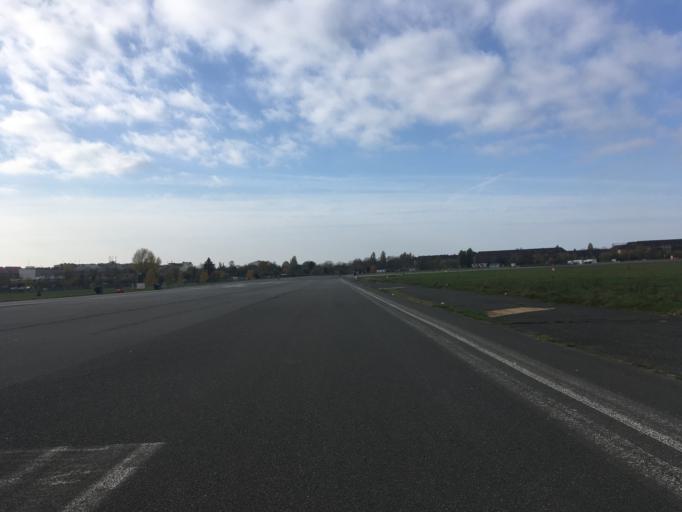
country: DE
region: Berlin
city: Tempelhof Bezirk
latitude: 52.4710
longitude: 13.3955
